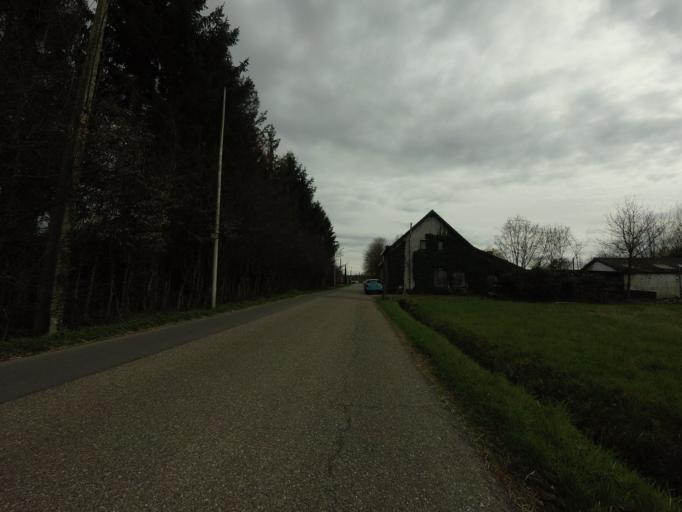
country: BE
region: Flanders
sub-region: Provincie Antwerpen
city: Lint
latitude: 51.1417
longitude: 4.5127
